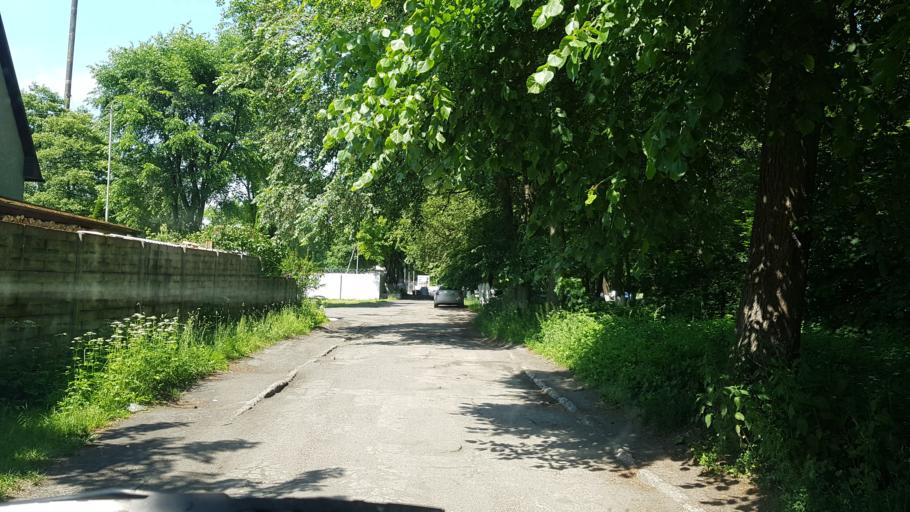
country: RU
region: Kaliningrad
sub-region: Gorod Kaliningrad
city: Baltiysk
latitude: 54.6484
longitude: 19.8892
